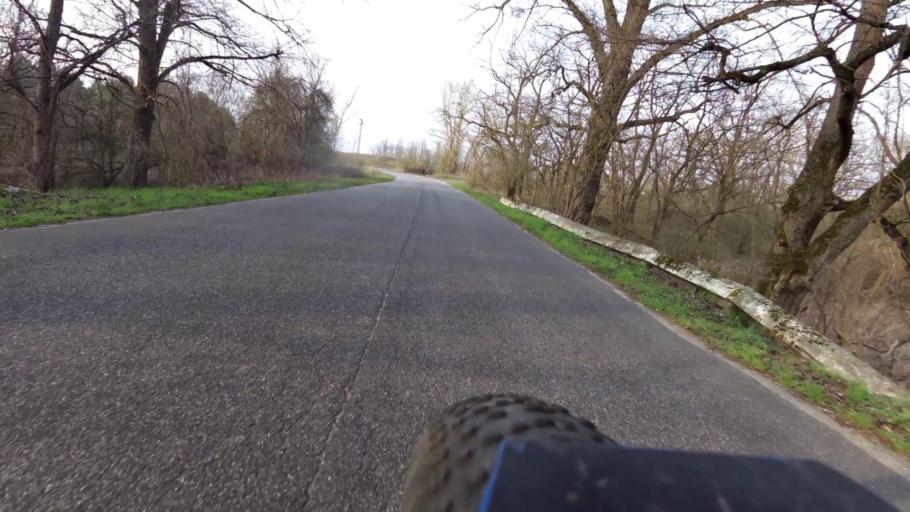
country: DE
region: Brandenburg
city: Vogelsang
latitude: 52.2521
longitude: 14.7041
